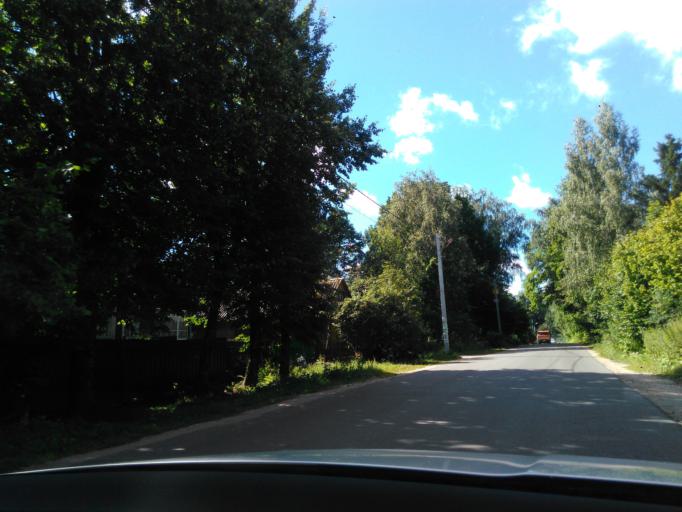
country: RU
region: Moskovskaya
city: Klin
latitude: 56.2320
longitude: 36.8189
